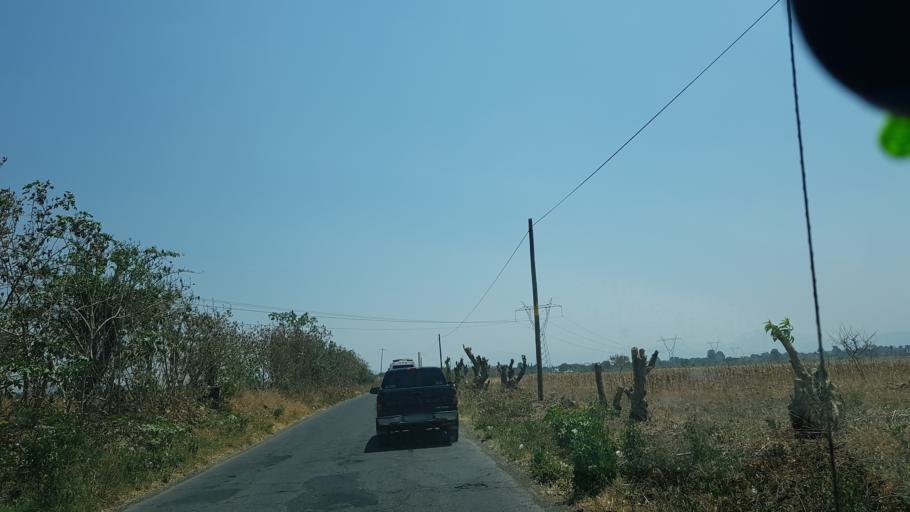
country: MX
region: Puebla
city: Tochimilco
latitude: 18.8892
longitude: -98.5269
